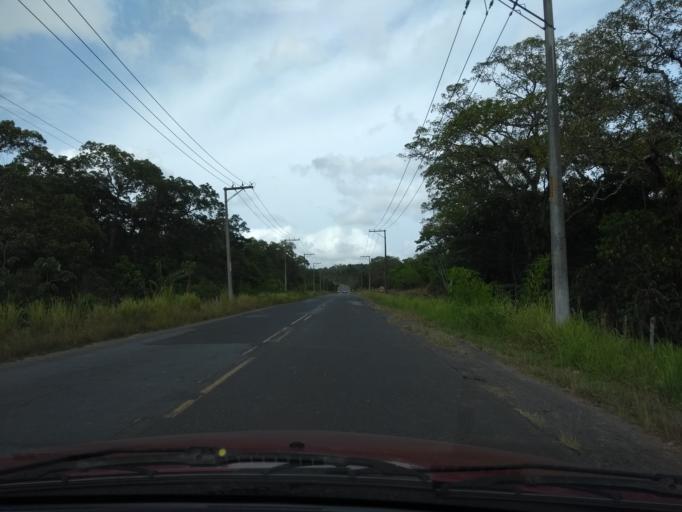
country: BR
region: Bahia
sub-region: Sao Francisco Do Conde
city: Sao Francisco do Conde
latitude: -12.6099
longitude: -38.6475
